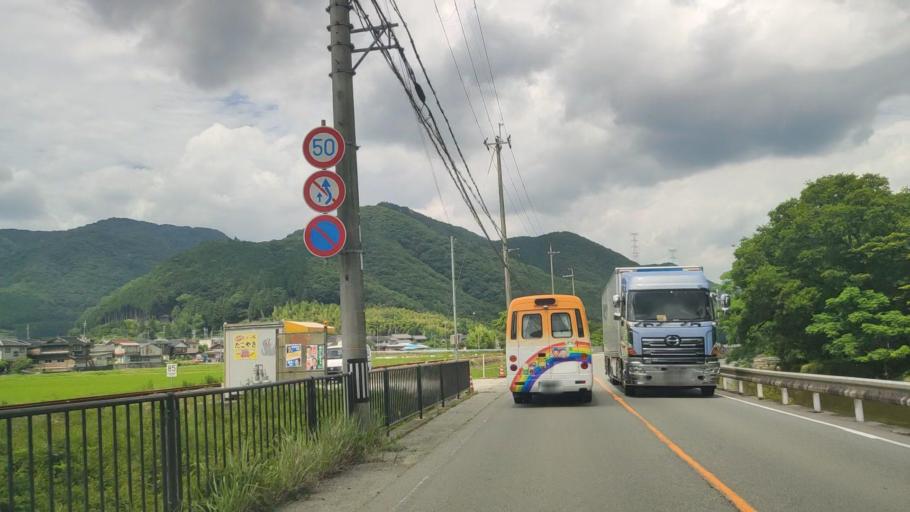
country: JP
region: Hyogo
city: Yamazakicho-nakabirose
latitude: 34.9401
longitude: 134.4870
